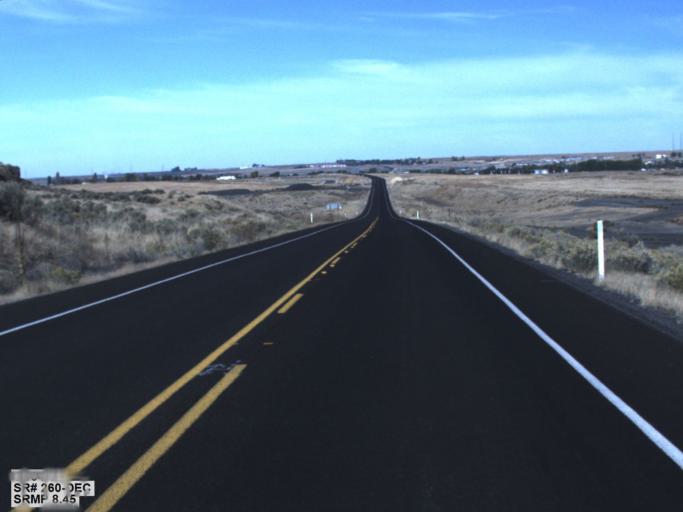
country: US
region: Washington
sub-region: Franklin County
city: Connell
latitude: 46.6461
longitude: -118.8367
